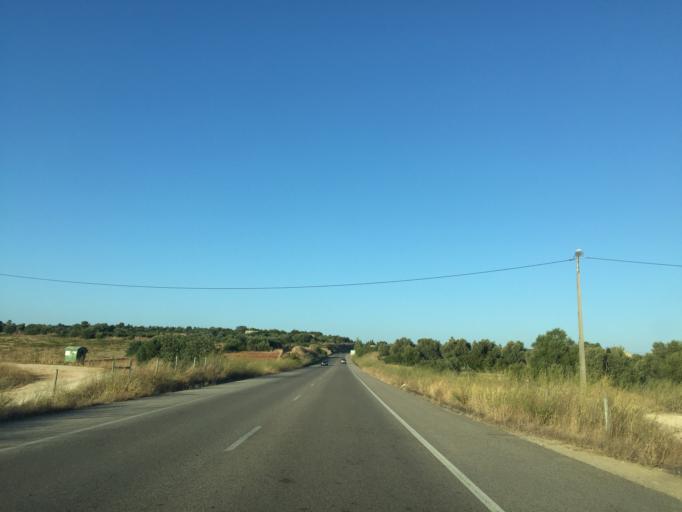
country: PT
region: Santarem
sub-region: Cartaxo
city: Pontevel
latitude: 39.1595
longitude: -8.8402
